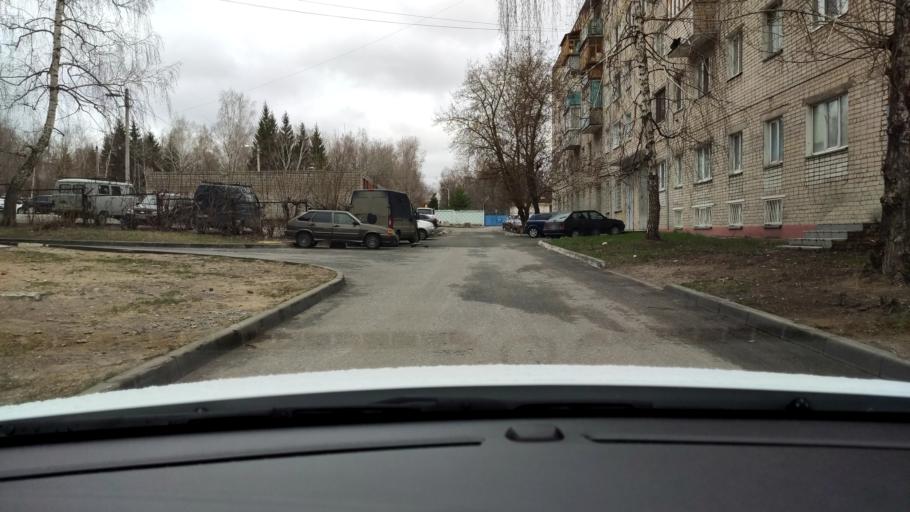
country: RU
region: Tatarstan
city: Vysokaya Gora
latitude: 55.8610
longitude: 49.2275
